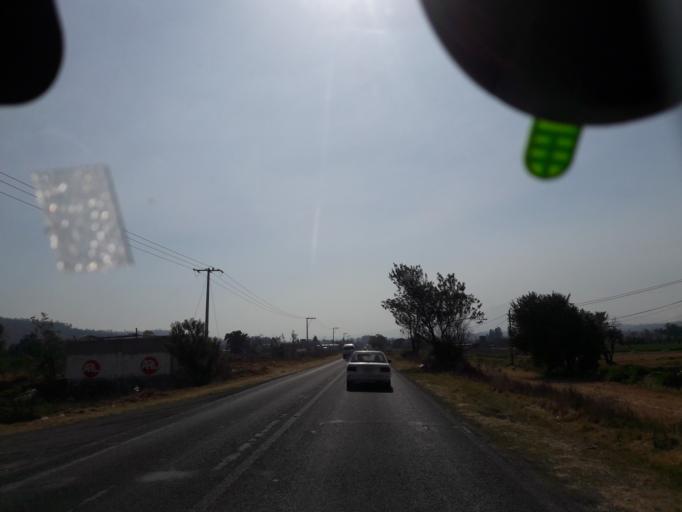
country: MX
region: Tlaxcala
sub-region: Panotla
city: Fraccionamiento la Virgen
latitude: 19.3216
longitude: -98.2996
